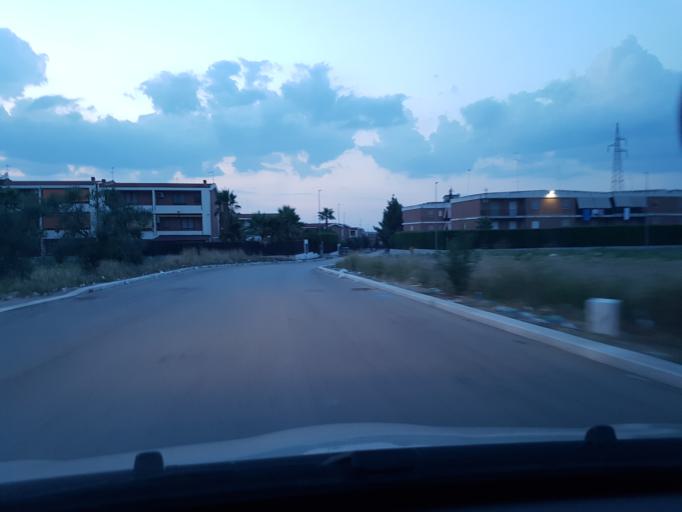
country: IT
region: Apulia
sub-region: Provincia di Foggia
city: Cerignola
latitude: 41.2596
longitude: 15.8806
